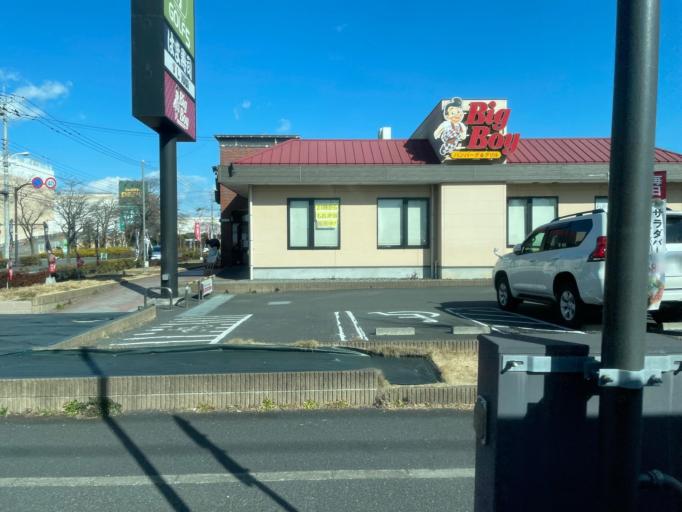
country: JP
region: Tokyo
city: Fussa
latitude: 35.7142
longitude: 139.3651
